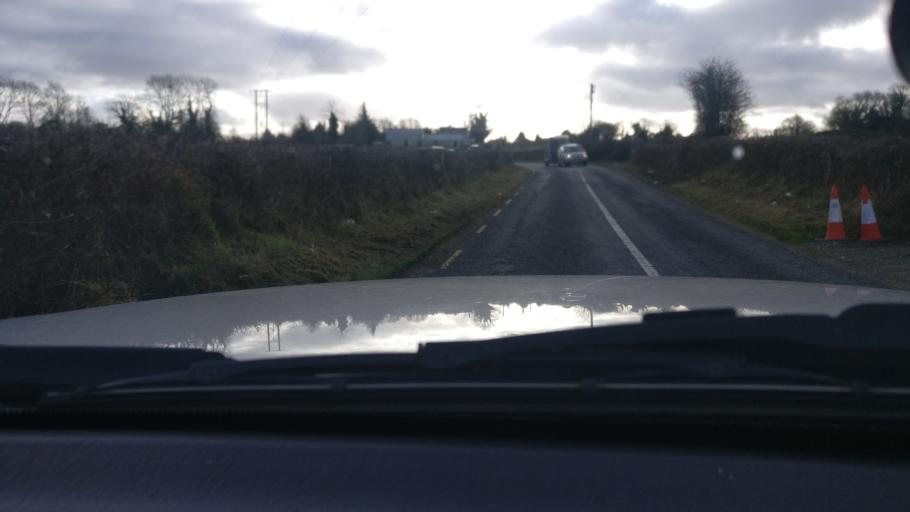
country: IE
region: Connaught
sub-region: County Galway
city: Ballinasloe
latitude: 53.2856
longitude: -8.2415
